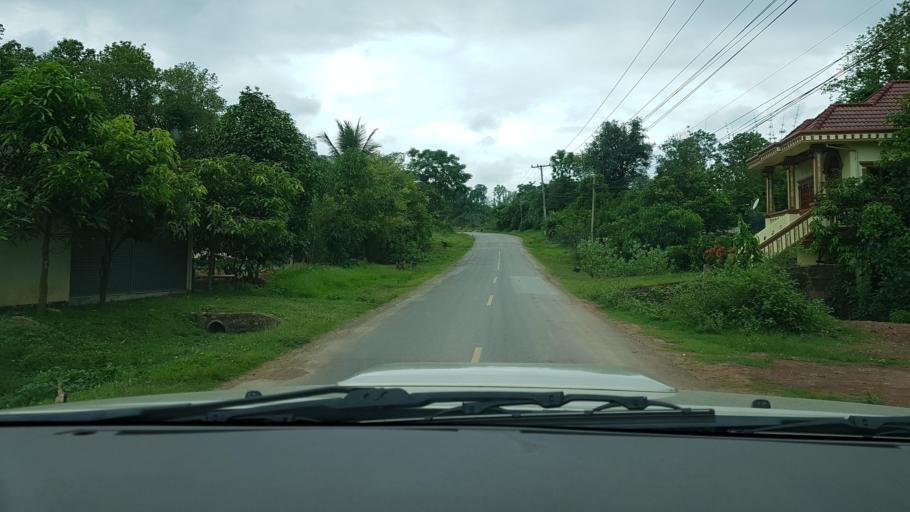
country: LA
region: Loungnamtha
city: Muang Nale
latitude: 20.3113
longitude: 101.6517
